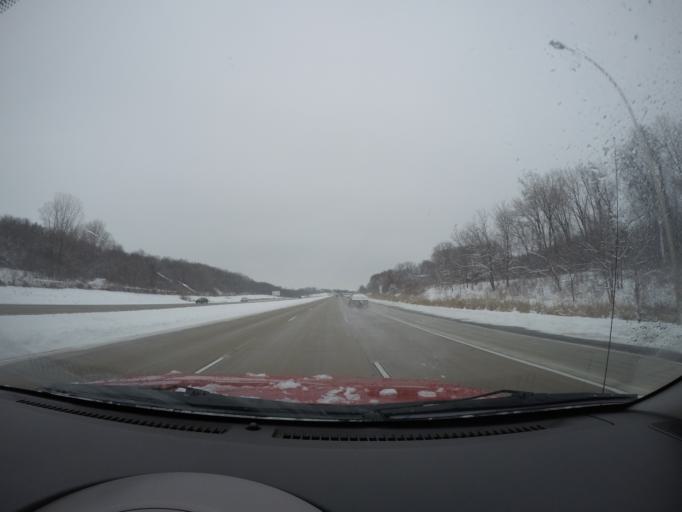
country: US
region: Minnesota
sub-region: Olmsted County
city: Rochester
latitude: 43.9787
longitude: -92.4686
